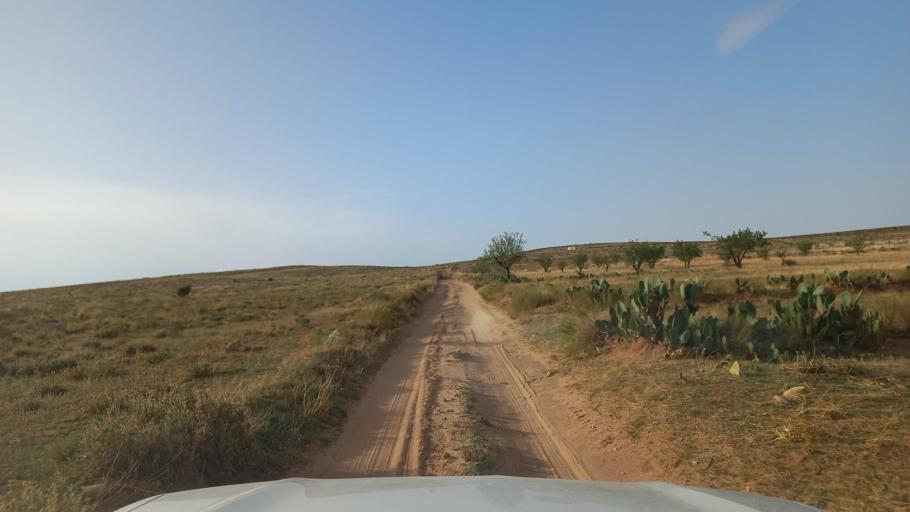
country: TN
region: Al Qasrayn
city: Kasserine
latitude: 35.3591
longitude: 8.8408
